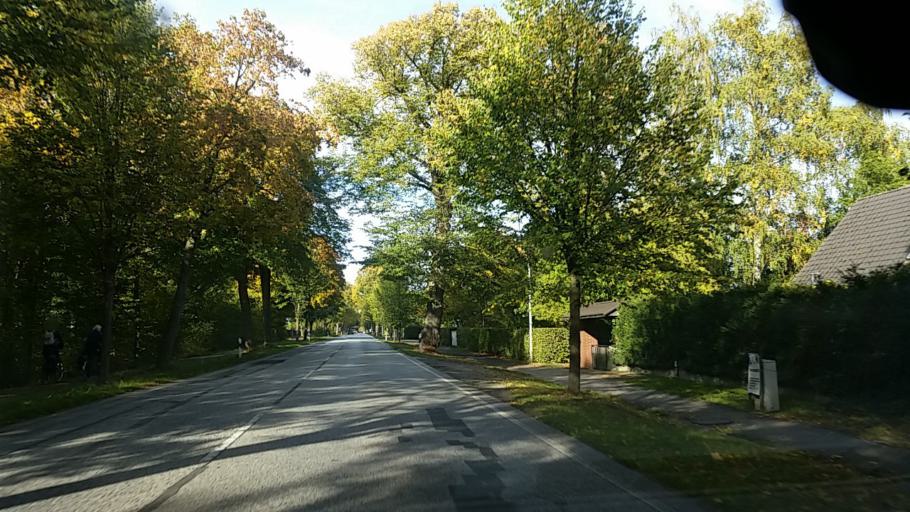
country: DE
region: Schleswig-Holstein
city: Delingsdorf
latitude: 53.6882
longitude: 10.2412
